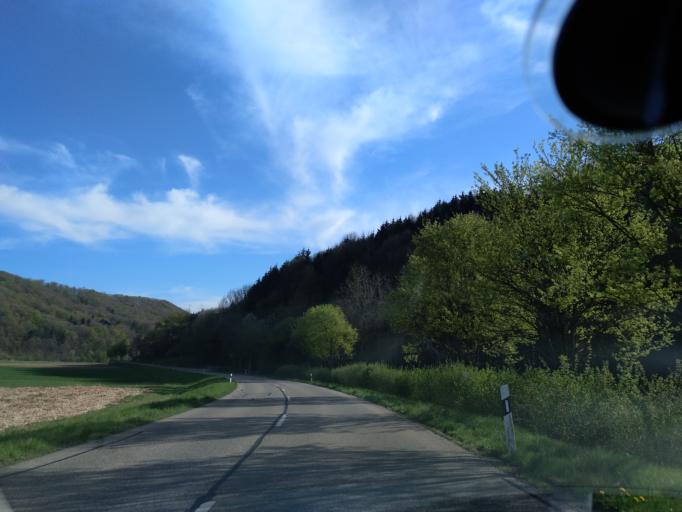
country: DE
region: Baden-Wuerttemberg
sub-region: Regierungsbezirk Stuttgart
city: Braunsbach
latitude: 49.1700
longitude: 9.7822
